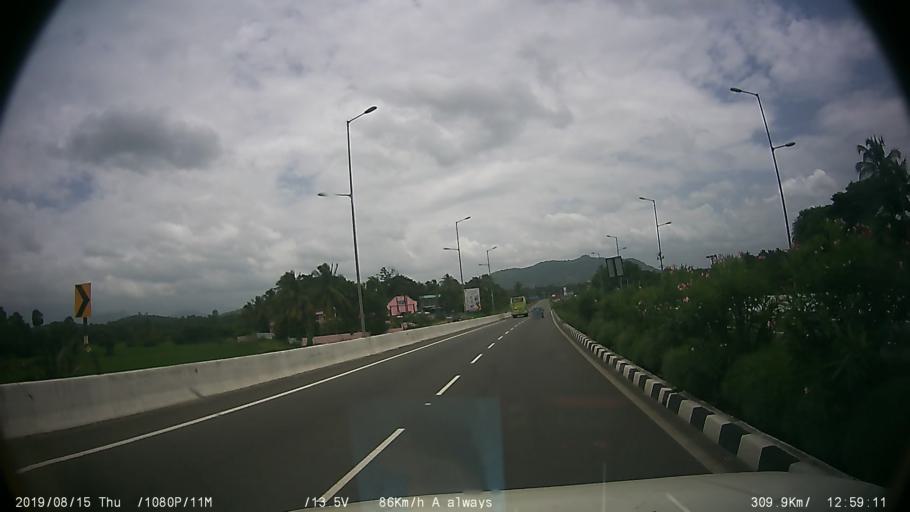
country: IN
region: Kerala
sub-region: Palakkad district
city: Palakkad
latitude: 10.6536
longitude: 76.5694
